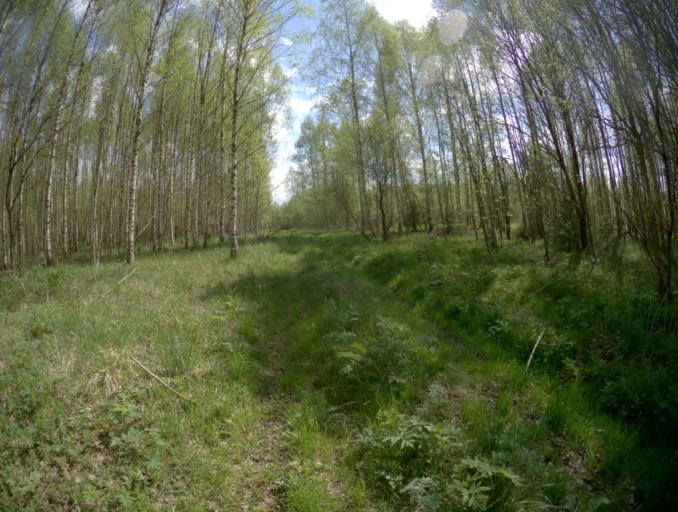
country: RU
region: Vladimir
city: Golovino
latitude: 55.9682
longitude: 40.3881
